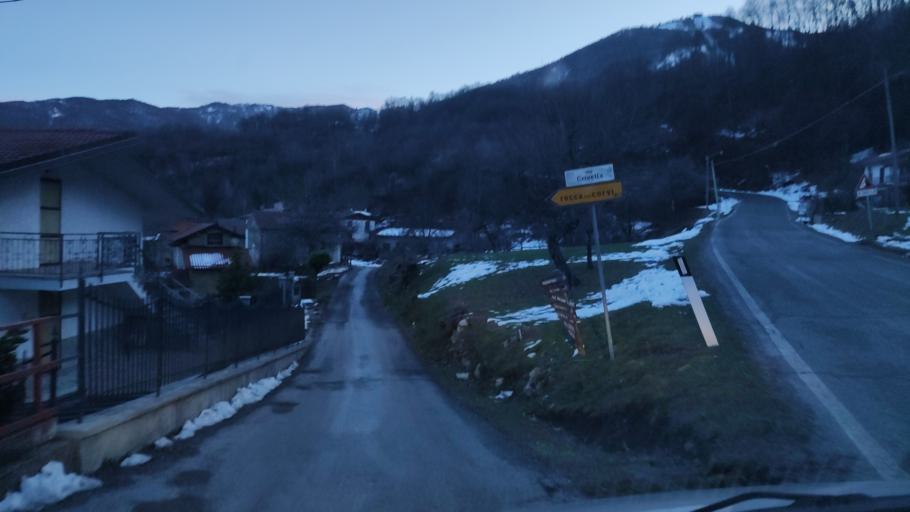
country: IT
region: Piedmont
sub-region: Provincia di Cuneo
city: Viola
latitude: 44.2837
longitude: 7.9596
